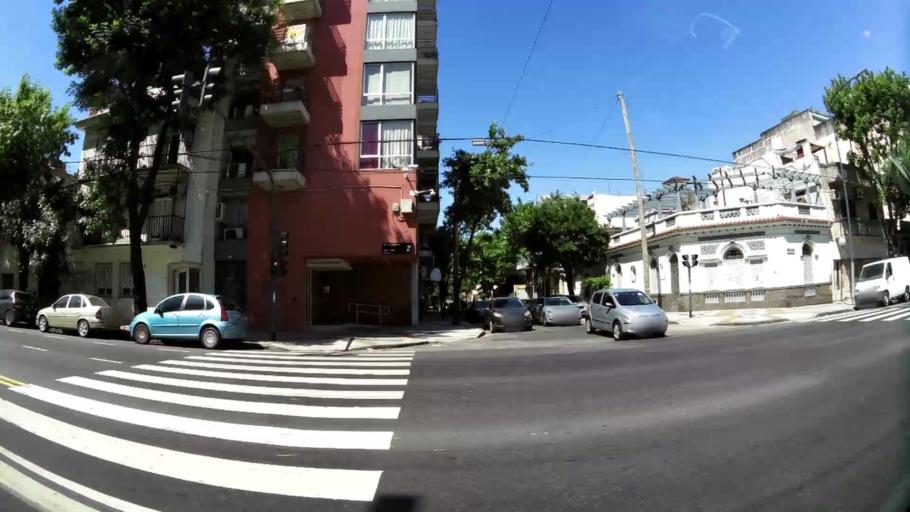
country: AR
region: Buenos Aires F.D.
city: Villa Santa Rita
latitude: -34.6325
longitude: -58.4537
